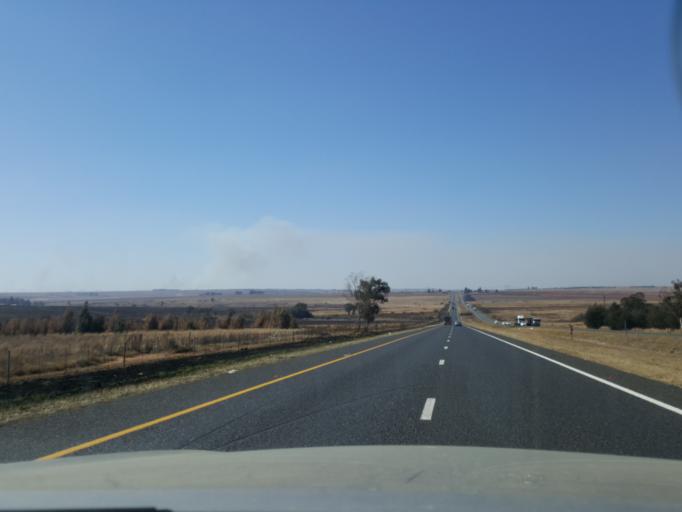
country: ZA
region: Mpumalanga
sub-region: Nkangala District Municipality
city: Delmas
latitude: -26.0359
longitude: 28.8544
